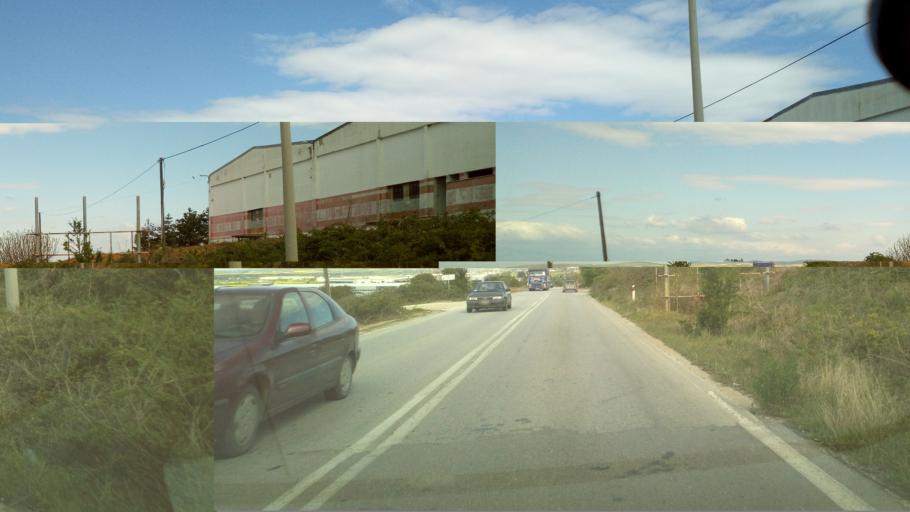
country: GR
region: Central Macedonia
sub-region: Nomos Kilkis
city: Nea Santa
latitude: 40.8229
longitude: 22.9275
